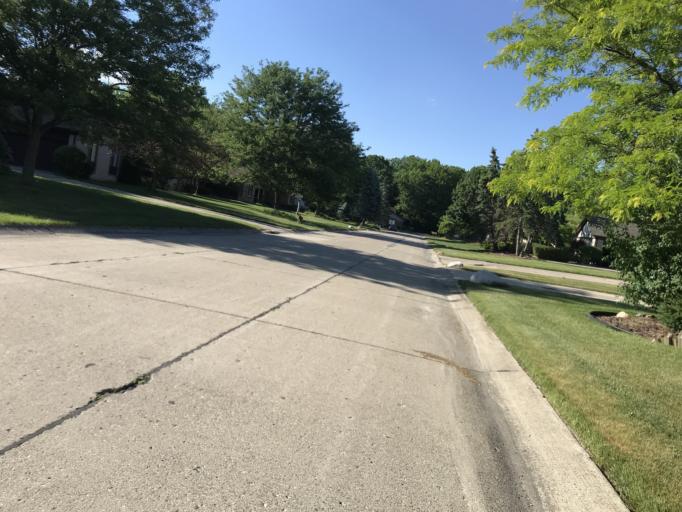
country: US
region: Michigan
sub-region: Oakland County
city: Farmington
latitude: 42.4750
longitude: -83.3471
